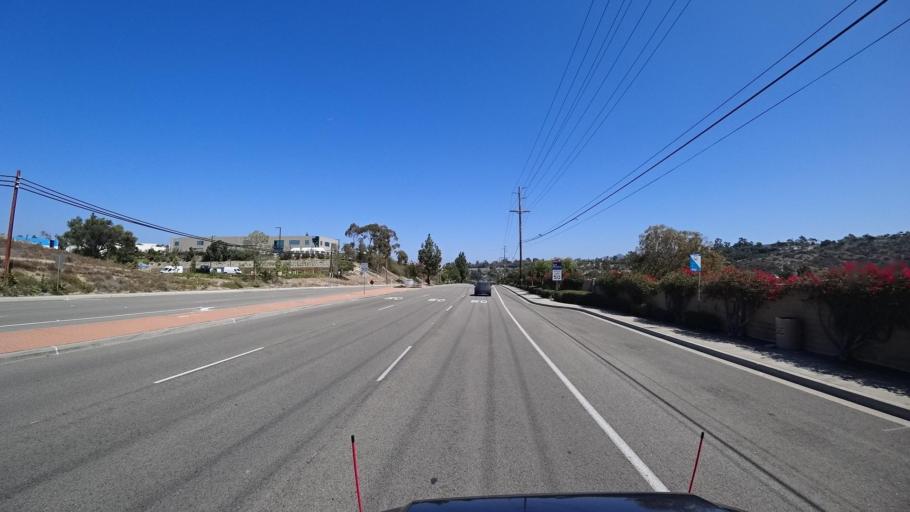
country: US
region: California
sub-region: San Diego County
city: Lake San Marcos
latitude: 33.1314
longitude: -117.2277
